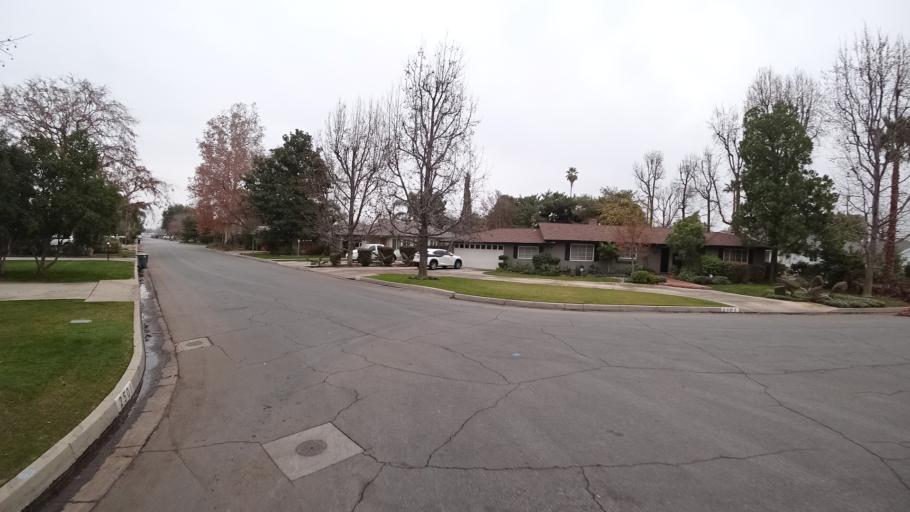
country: US
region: California
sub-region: Kern County
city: Bakersfield
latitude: 35.3827
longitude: -119.0283
